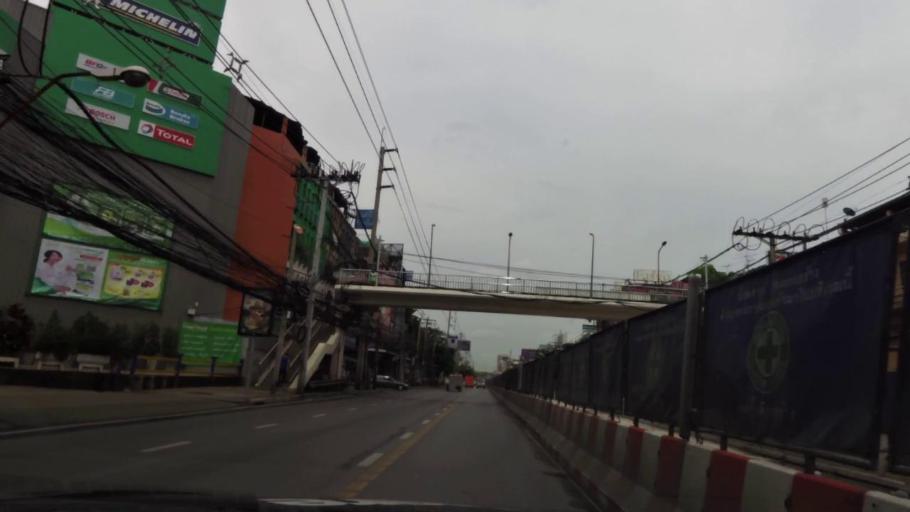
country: TH
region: Bangkok
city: Bang Kapi
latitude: 13.7719
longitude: 100.6348
